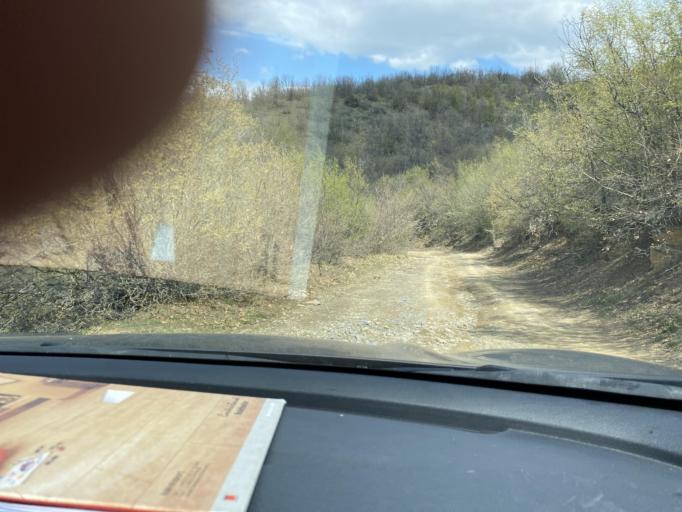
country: MK
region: Caska
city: Caska
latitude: 41.7316
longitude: 21.6546
